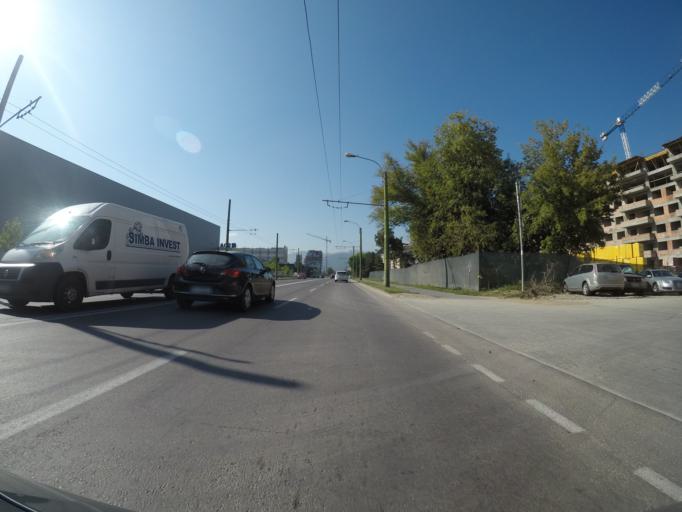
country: RO
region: Brasov
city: Brasov
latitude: 45.6767
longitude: 25.6132
